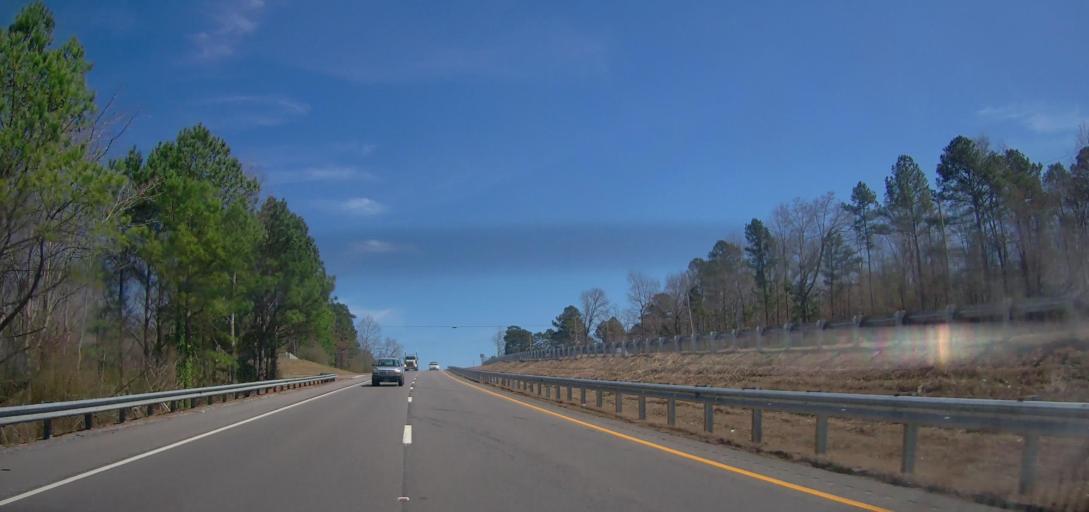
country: US
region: Alabama
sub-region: Cullman County
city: Cullman
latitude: 34.1820
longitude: -86.7670
